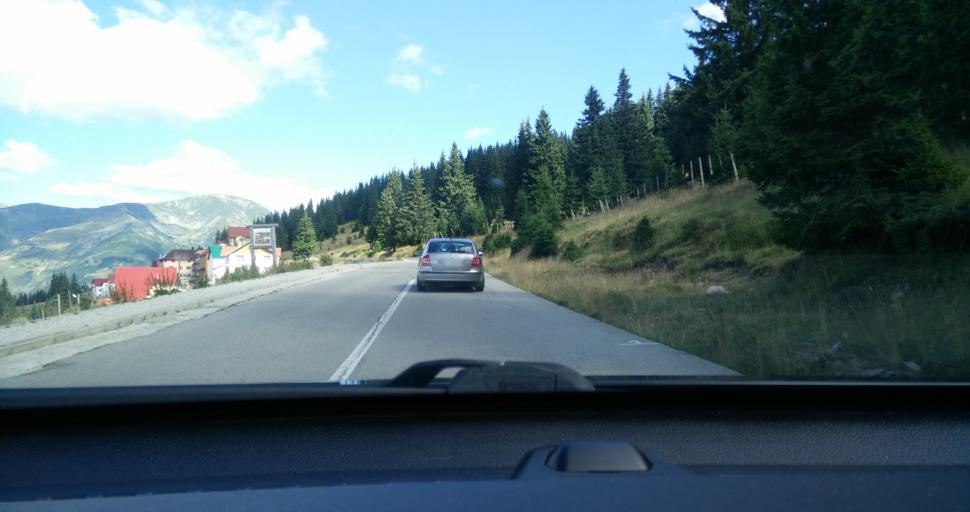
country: RO
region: Gorj
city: Novaci-Straini
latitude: 45.2943
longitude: 23.6853
